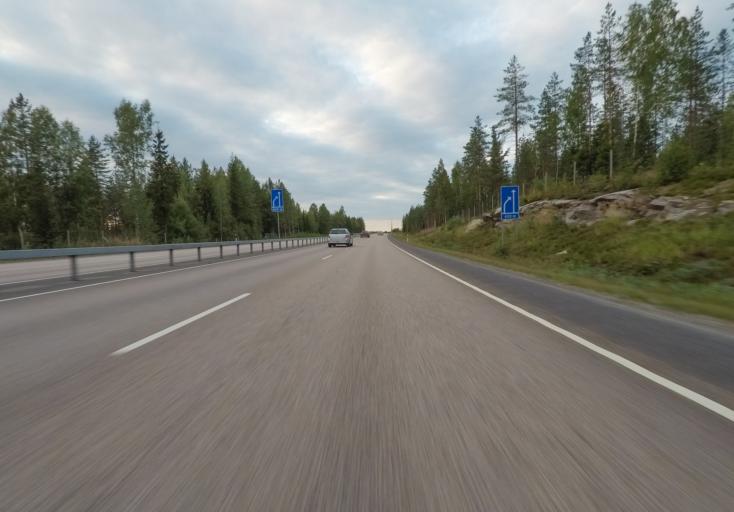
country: FI
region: Central Finland
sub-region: Joutsa
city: Leivonmaeki
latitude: 61.9830
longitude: 26.0621
